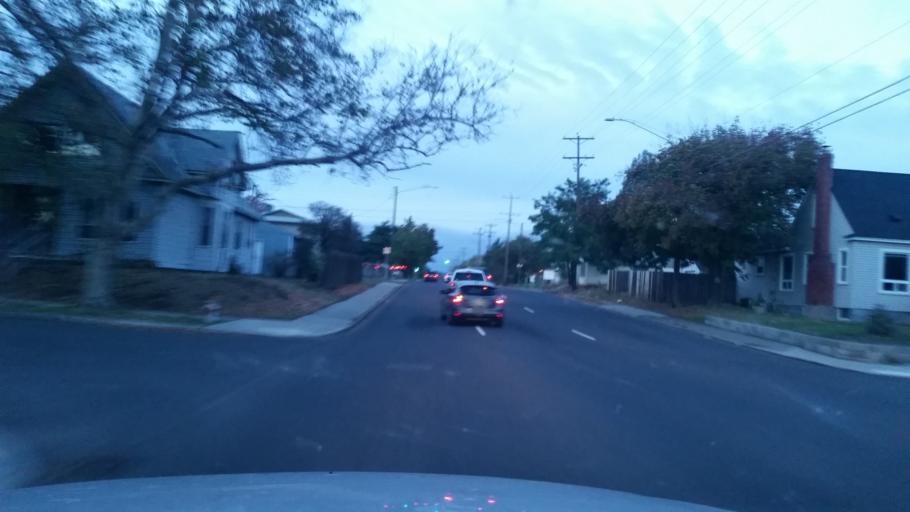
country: US
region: Washington
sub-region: Spokane County
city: Spokane
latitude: 47.6730
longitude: -117.4356
